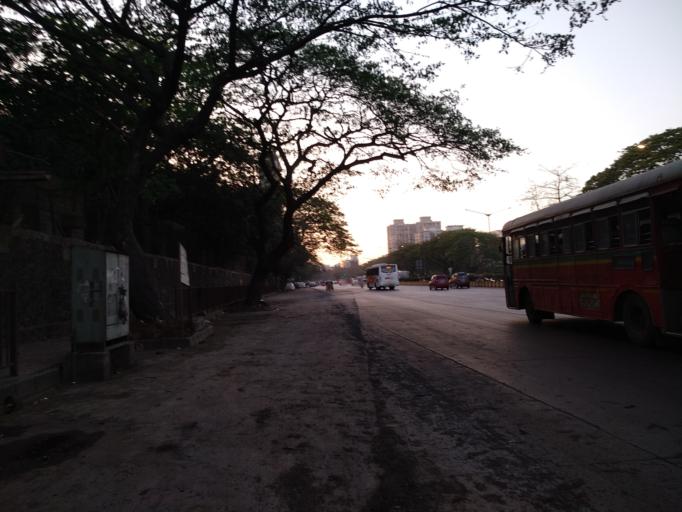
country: IN
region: Maharashtra
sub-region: Mumbai Suburban
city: Mumbai
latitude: 19.0438
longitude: 72.9205
